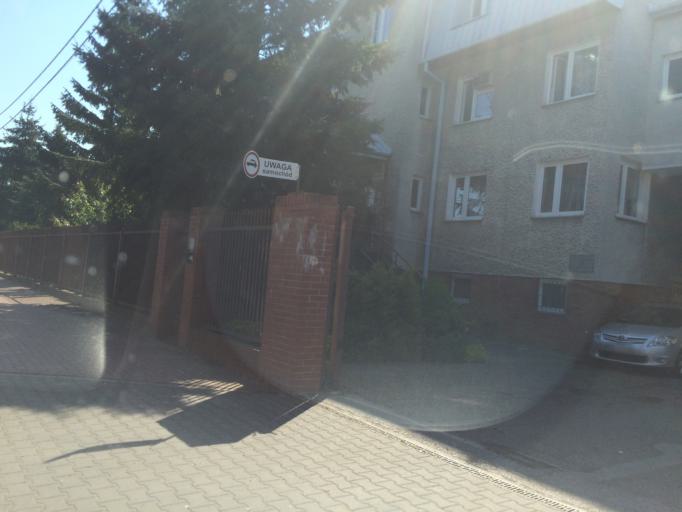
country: PL
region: Masovian Voivodeship
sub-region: Powiat wolominski
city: Zabki
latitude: 52.2998
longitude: 21.0972
